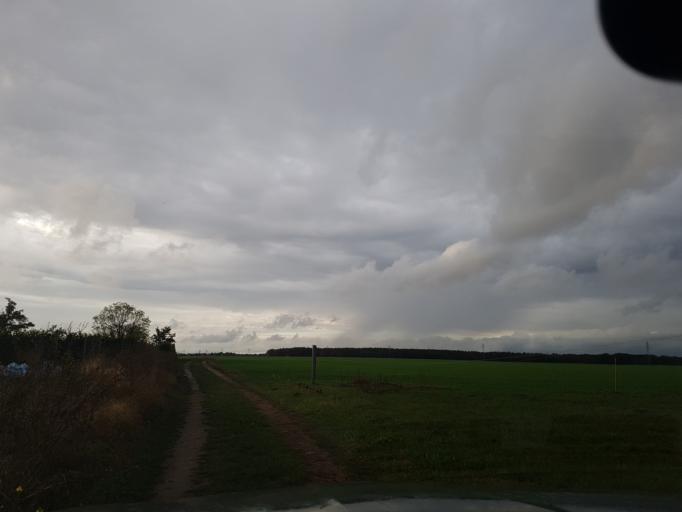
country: DE
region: Brandenburg
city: Falkenberg
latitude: 51.5439
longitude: 13.2814
